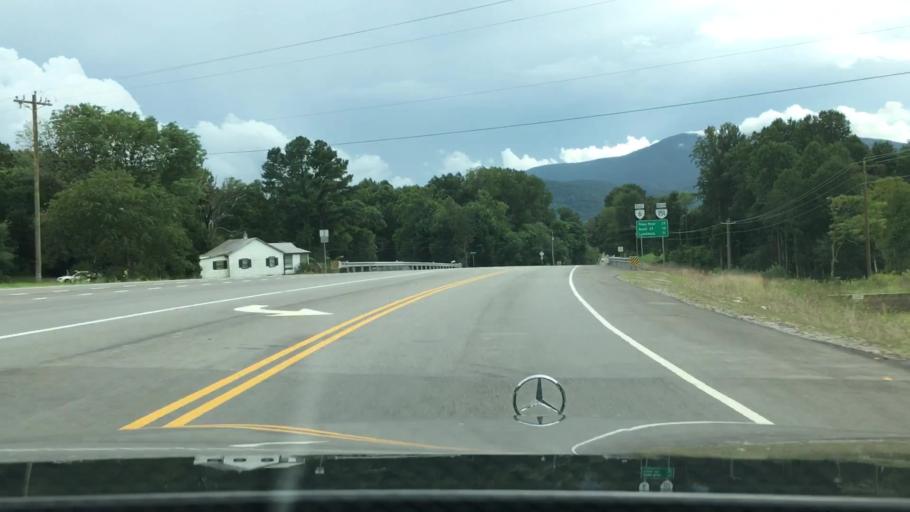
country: US
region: Virginia
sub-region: City of Waynesboro
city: Waynesboro
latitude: 37.9997
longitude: -78.8272
